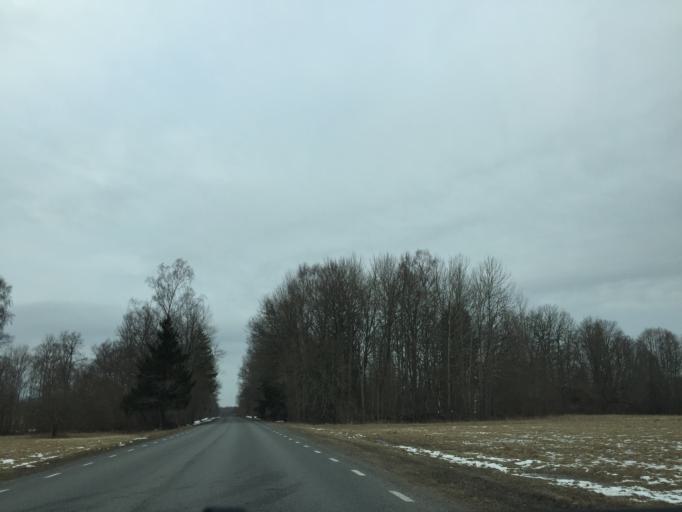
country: EE
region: Saare
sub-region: Kuressaare linn
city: Kuressaare
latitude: 58.4562
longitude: 22.2408
